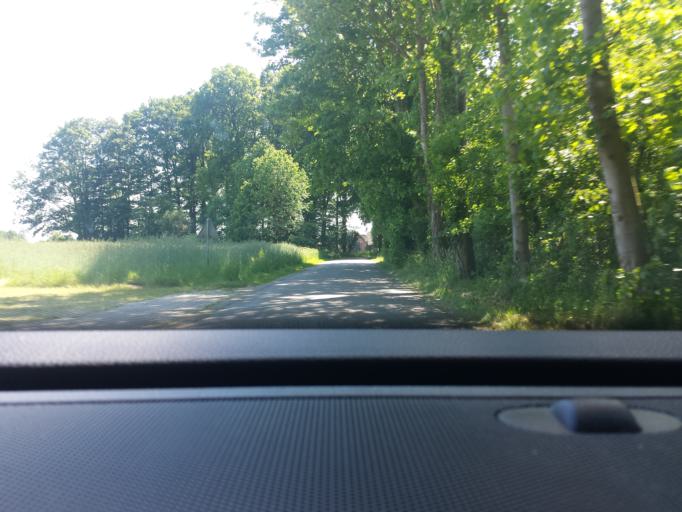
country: NL
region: Gelderland
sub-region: Gemeente Lochem
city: Almen
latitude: 52.1223
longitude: 6.3143
